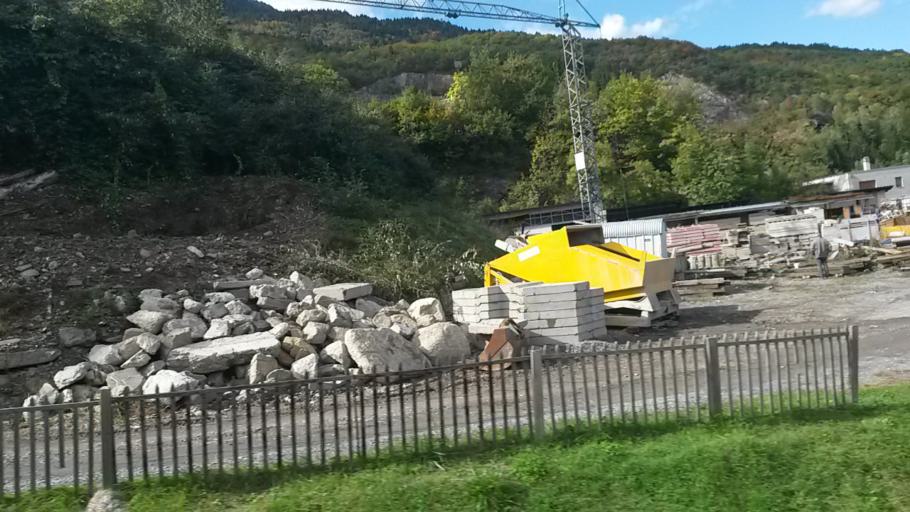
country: CH
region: Valais
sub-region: Monthey District
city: Collombey
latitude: 46.2554
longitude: 6.9424
